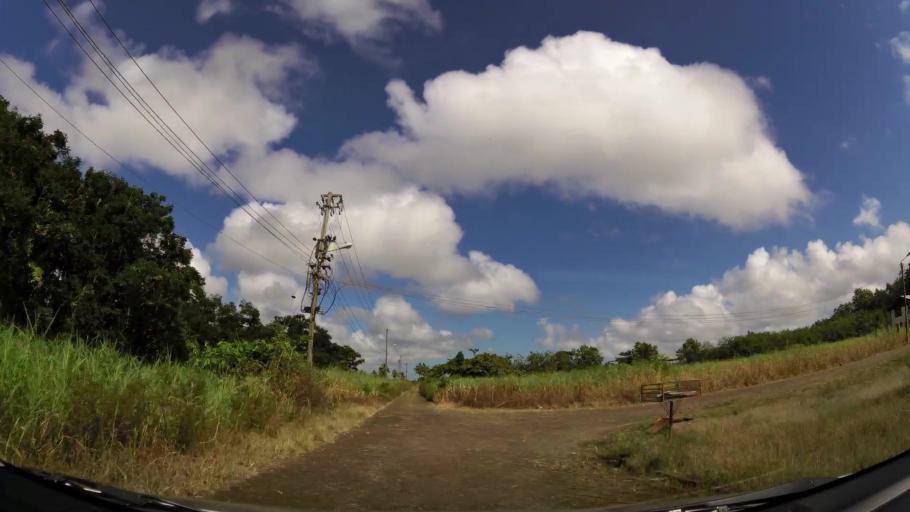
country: SR
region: Commewijne
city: Nieuw Amsterdam
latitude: 5.8781
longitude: -55.1129
